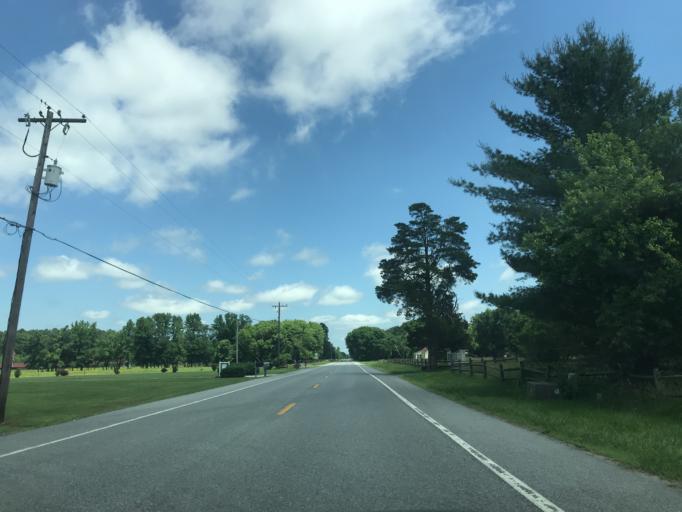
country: US
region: Maryland
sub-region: Caroline County
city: Federalsburg
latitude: 38.7093
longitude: -75.7478
